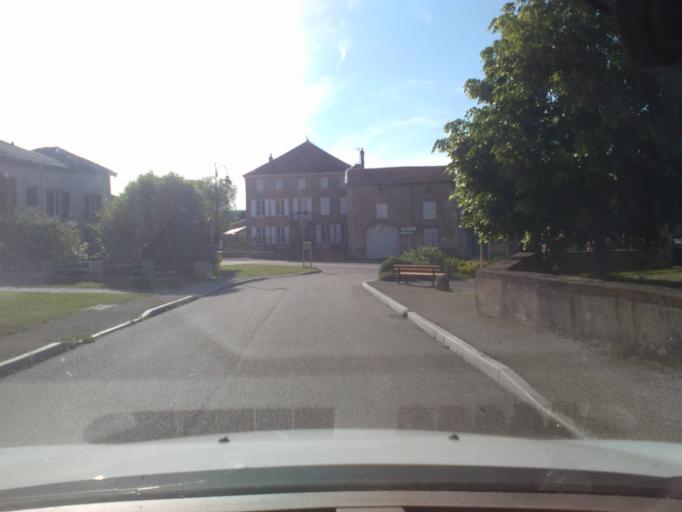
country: FR
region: Lorraine
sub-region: Departement des Vosges
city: Mirecourt
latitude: 48.2660
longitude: 6.2273
